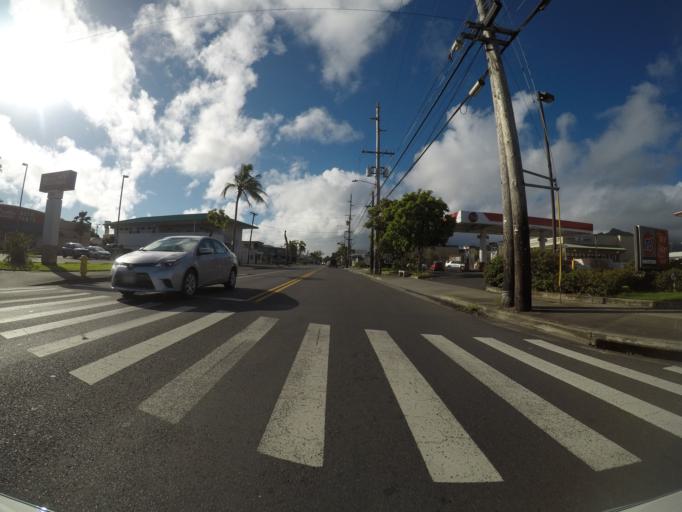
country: US
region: Hawaii
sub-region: Honolulu County
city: Kailua
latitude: 21.3969
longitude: -157.7460
